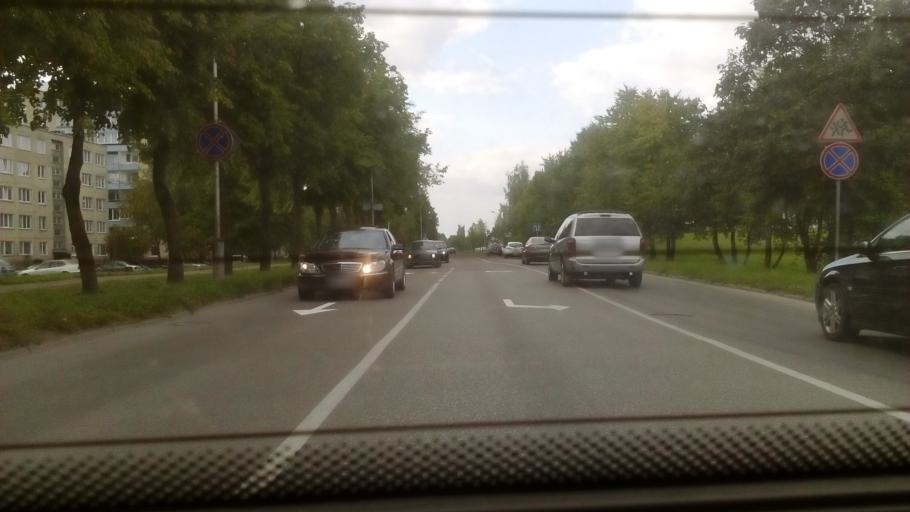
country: LT
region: Alytaus apskritis
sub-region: Alytus
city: Alytus
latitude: 54.4102
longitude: 24.0253
